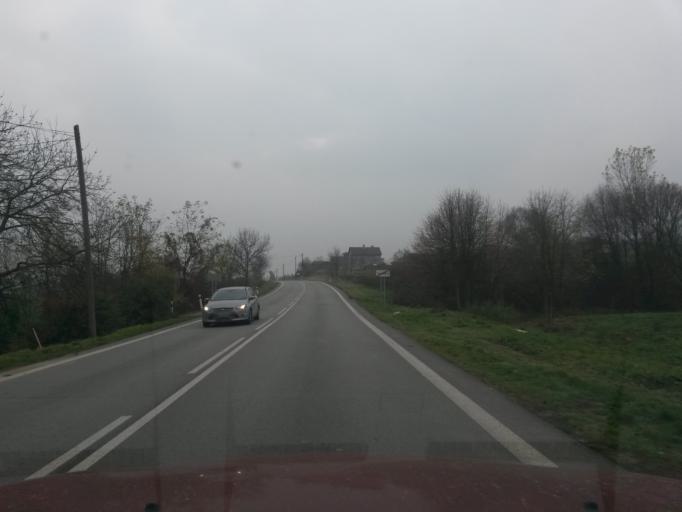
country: SK
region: Kosicky
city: Kosice
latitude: 48.8415
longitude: 21.2804
